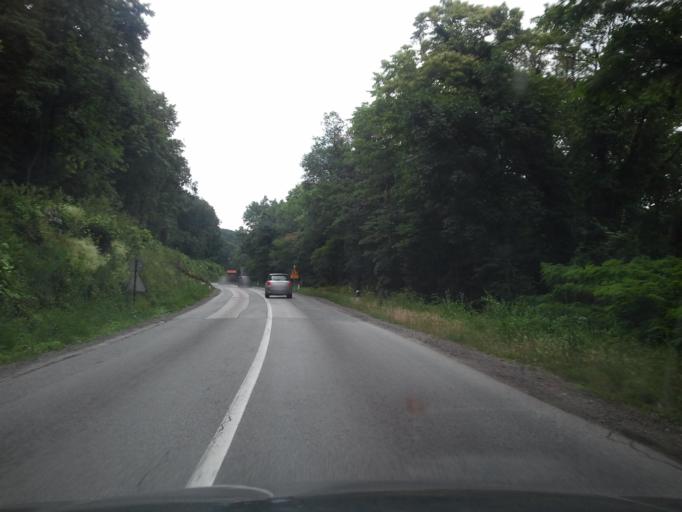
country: RS
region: Autonomna Pokrajina Vojvodina
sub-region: Sremski Okrug
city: Irig
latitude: 45.1377
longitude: 19.8374
